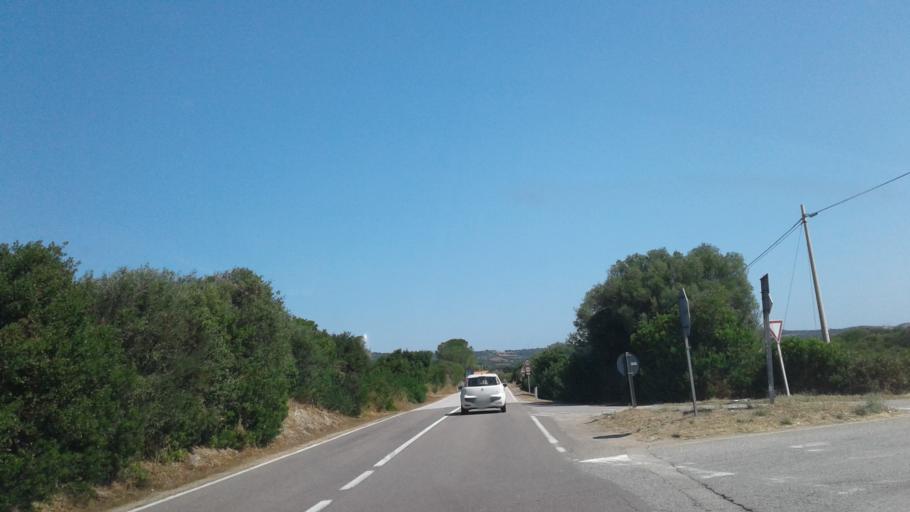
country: IT
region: Sardinia
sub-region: Provincia di Olbia-Tempio
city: Luogosanto
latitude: 41.1121
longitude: 9.2625
